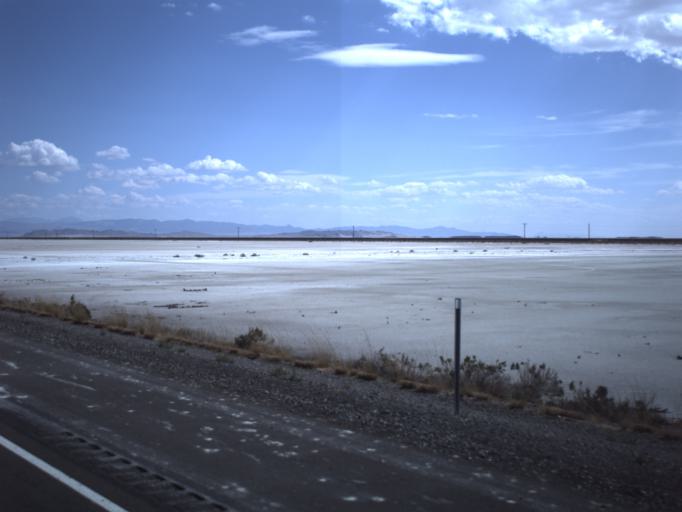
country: US
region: Utah
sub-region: Tooele County
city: Wendover
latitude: 40.7301
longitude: -113.4666
